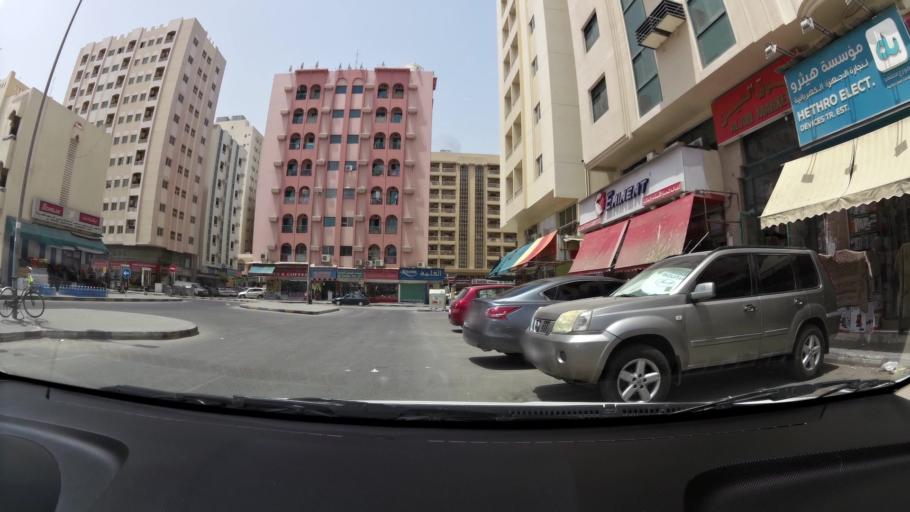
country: AE
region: Ash Shariqah
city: Sharjah
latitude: 25.3584
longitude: 55.3914
